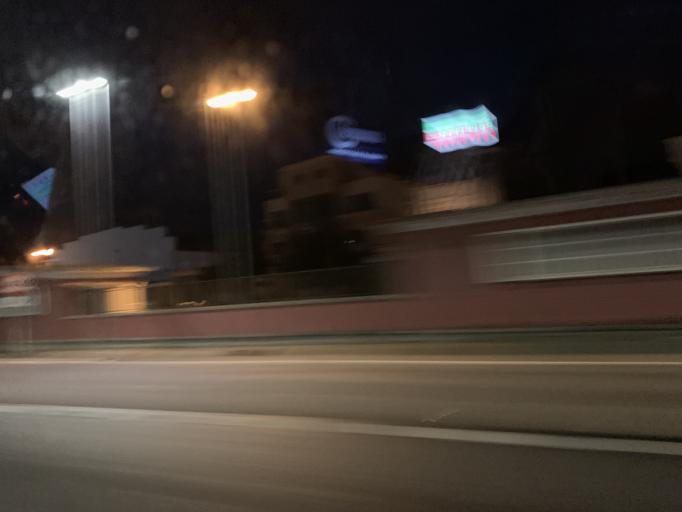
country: ES
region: Extremadura
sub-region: Provincia de Badajoz
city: Badajoz
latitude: 38.8835
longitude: -6.9340
